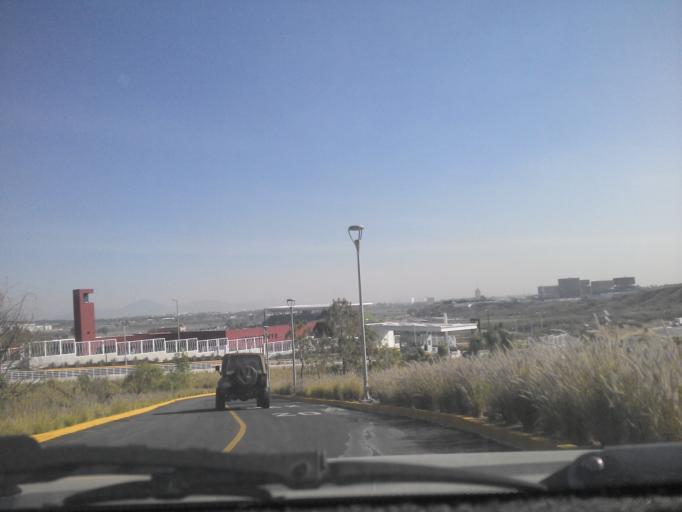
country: MX
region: Jalisco
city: Guadalajara
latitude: 20.6697
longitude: -103.4635
